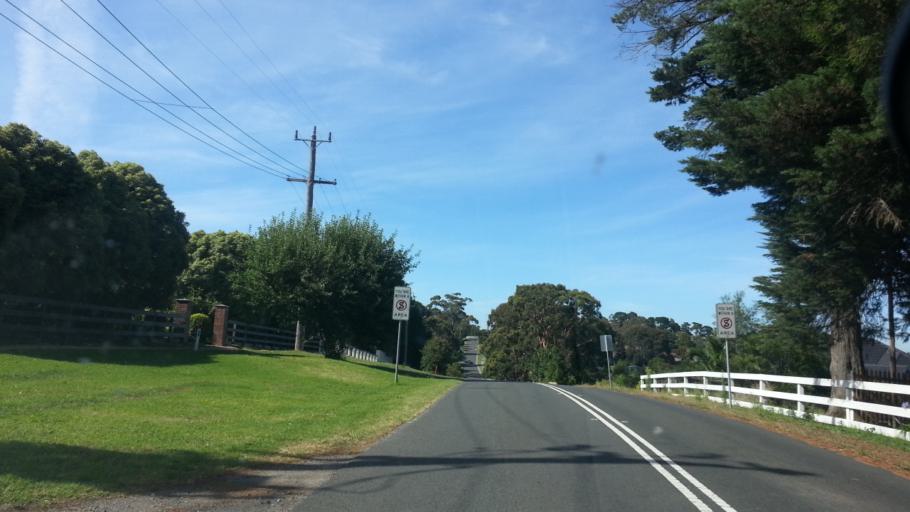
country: AU
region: Victoria
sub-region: Yarra Ranges
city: Lysterfield
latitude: -37.9576
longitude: 145.2829
